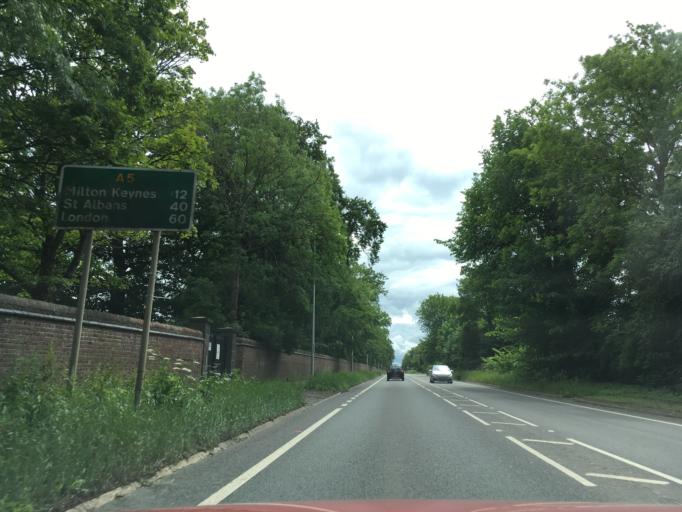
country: GB
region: England
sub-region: Northamptonshire
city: Towcester
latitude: 52.1264
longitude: -0.9801
